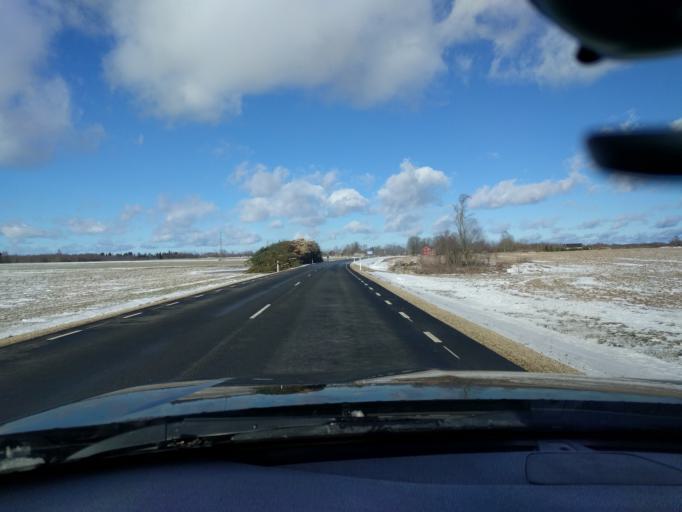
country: EE
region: Harju
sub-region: Raasiku vald
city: Raasiku
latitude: 59.2946
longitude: 25.1783
